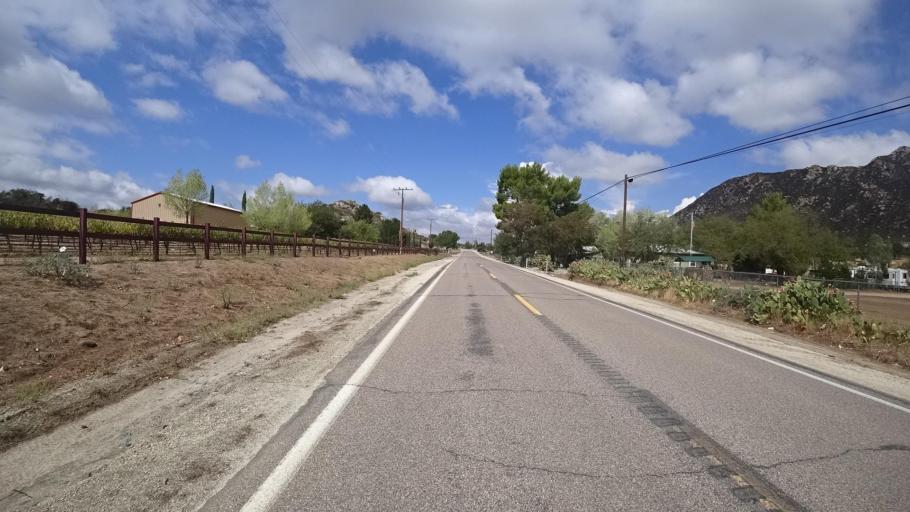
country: US
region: California
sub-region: San Diego County
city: Campo
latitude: 32.6758
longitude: -116.4887
